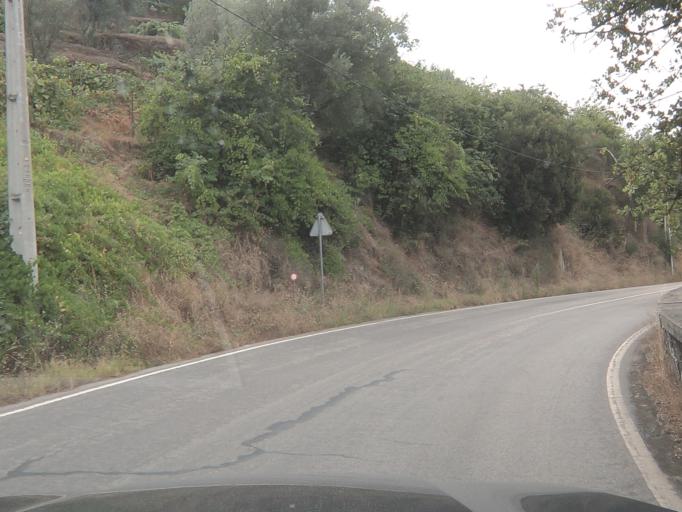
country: PT
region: Vila Real
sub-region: Santa Marta de Penaguiao
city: Santa Marta de Penaguiao
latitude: 41.2381
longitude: -7.7642
